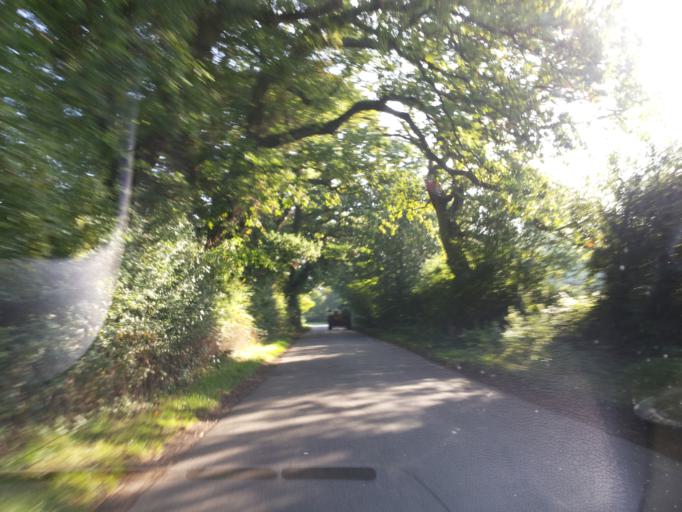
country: GB
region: England
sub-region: Warwickshire
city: Wroxall
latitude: 52.3285
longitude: -1.6694
